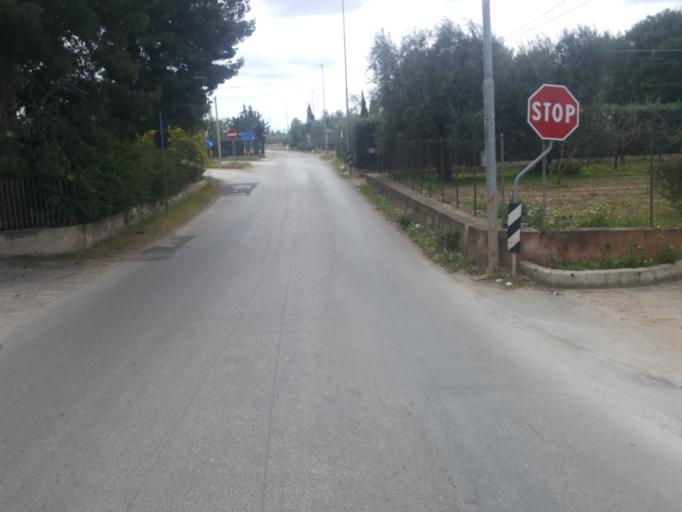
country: IT
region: Apulia
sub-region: Provincia di Barletta - Andria - Trani
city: Bisceglie
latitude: 41.2223
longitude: 16.5054
